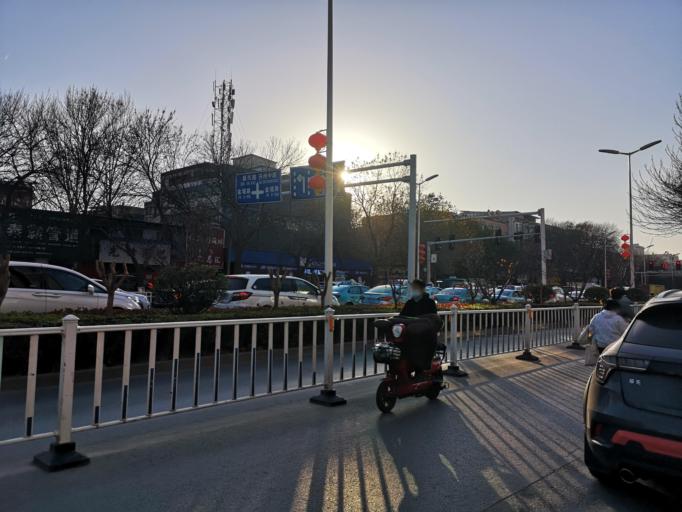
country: CN
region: Henan Sheng
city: Puyang
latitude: 35.7723
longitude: 115.0333
